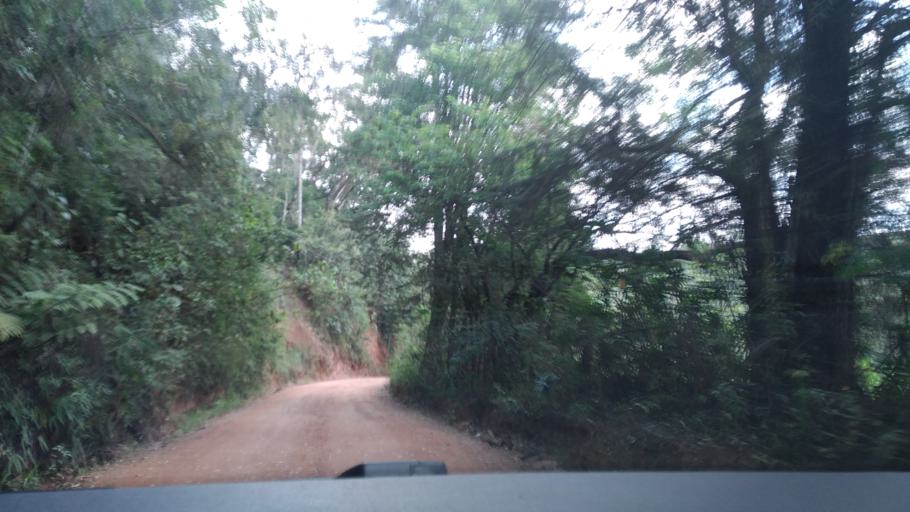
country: BR
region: Sao Paulo
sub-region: Cajamar
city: Cajamar
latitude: -23.2858
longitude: -46.8896
